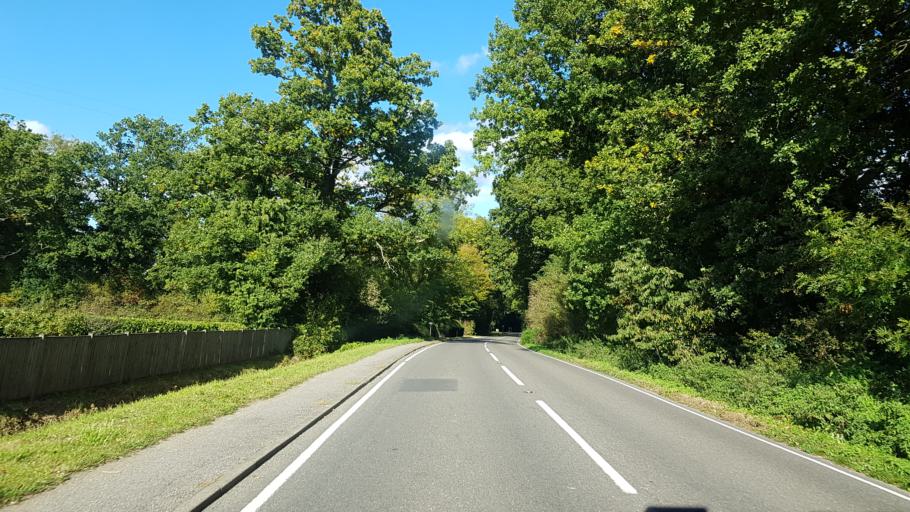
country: GB
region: England
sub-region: Surrey
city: Chiddingfold
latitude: 51.0896
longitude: -0.6449
